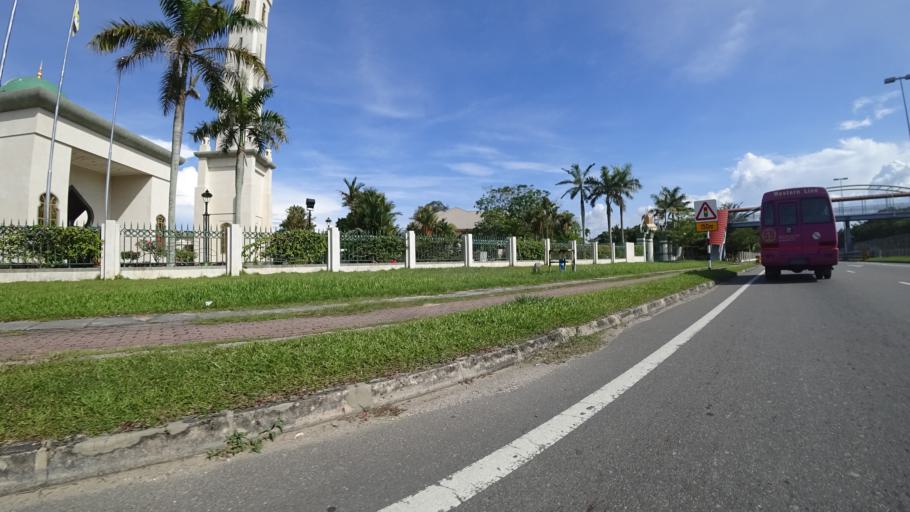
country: BN
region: Brunei and Muara
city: Bandar Seri Begawan
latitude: 4.9388
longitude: 114.8421
